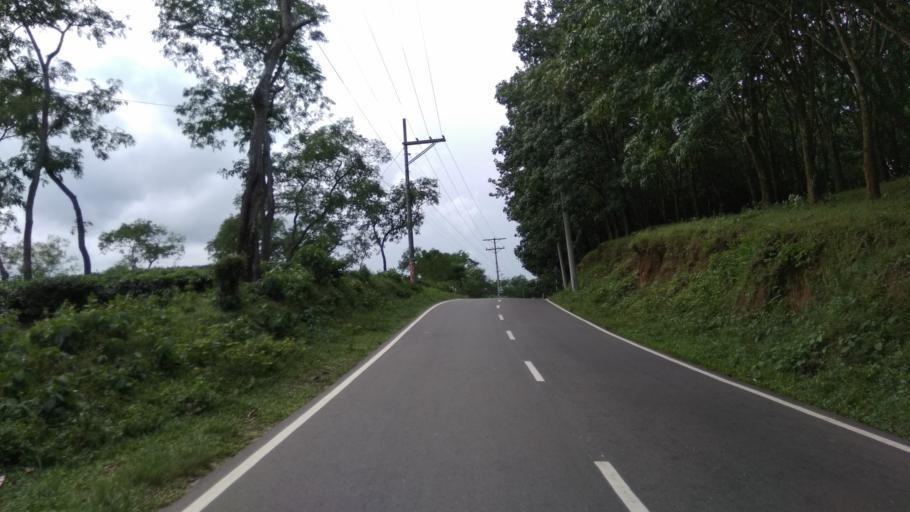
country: IN
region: Tripura
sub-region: Dhalai
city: Kamalpur
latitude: 24.2998
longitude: 91.7570
